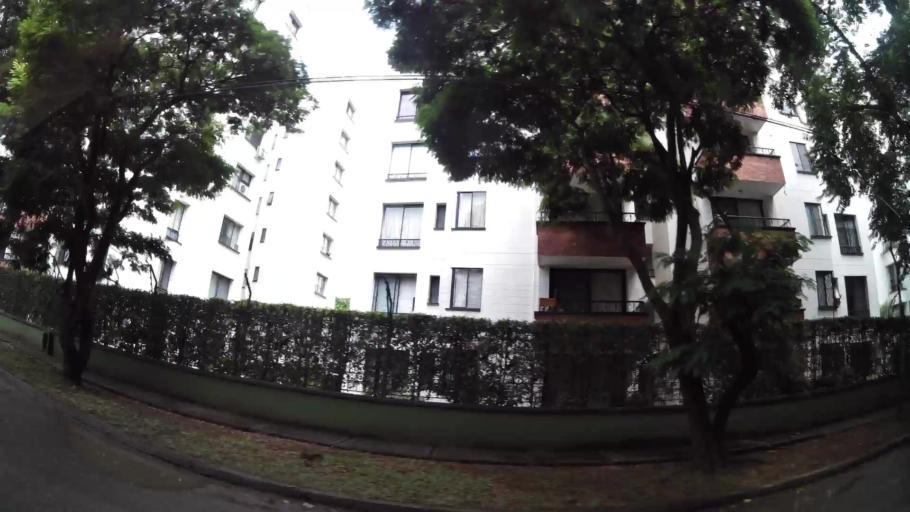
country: CO
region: Valle del Cauca
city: Cali
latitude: 3.3961
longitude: -76.5360
